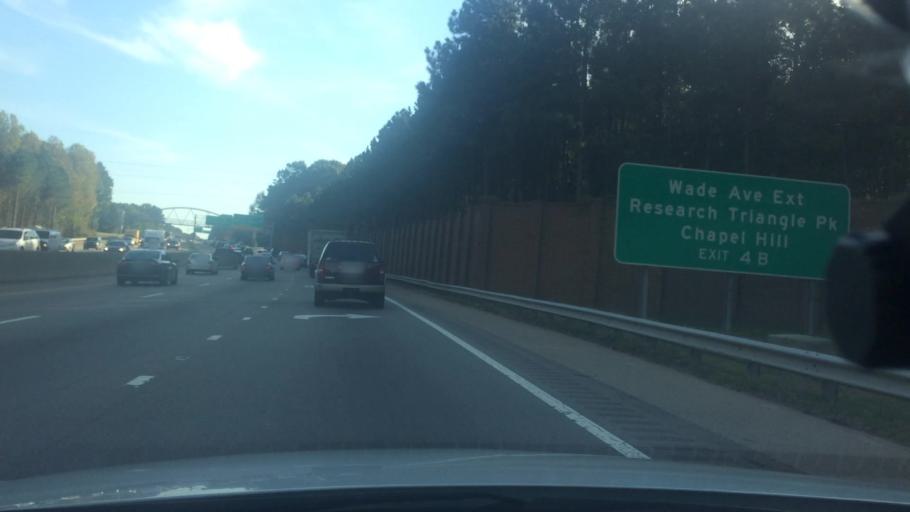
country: US
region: North Carolina
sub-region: Wake County
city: West Raleigh
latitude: 35.8099
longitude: -78.6939
